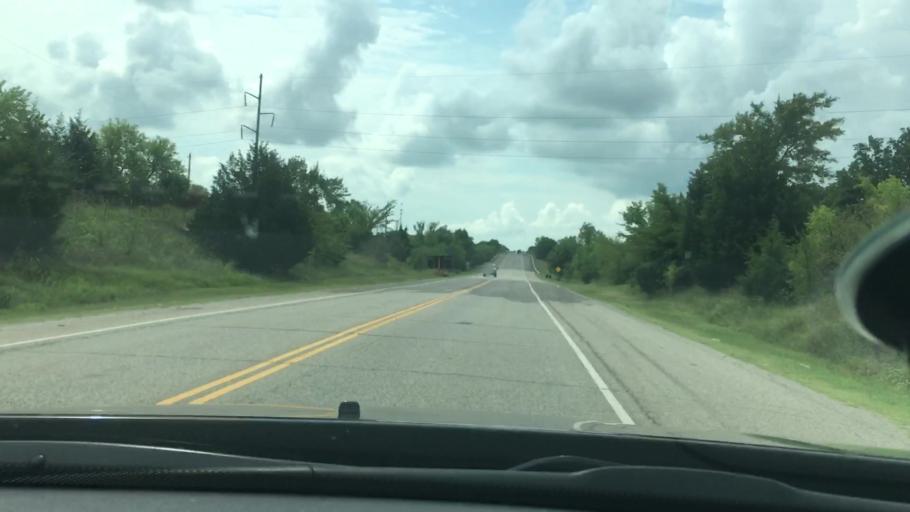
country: US
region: Oklahoma
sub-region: Carter County
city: Ardmore
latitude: 34.1973
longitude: -97.1082
